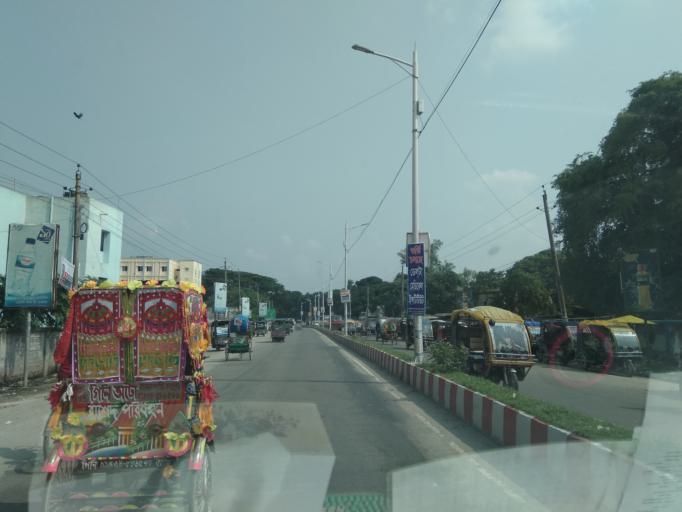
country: BD
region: Rangpur Division
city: Rangpur
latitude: 25.7683
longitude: 89.2296
